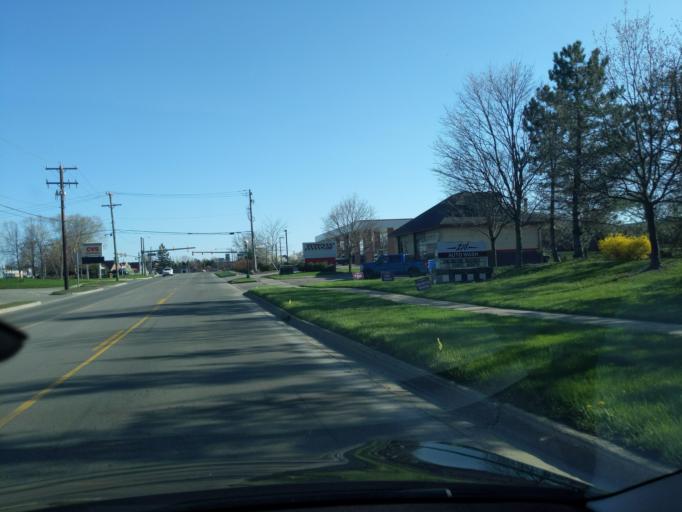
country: US
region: Michigan
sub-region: Washtenaw County
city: Chelsea
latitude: 42.3082
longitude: -84.0212
